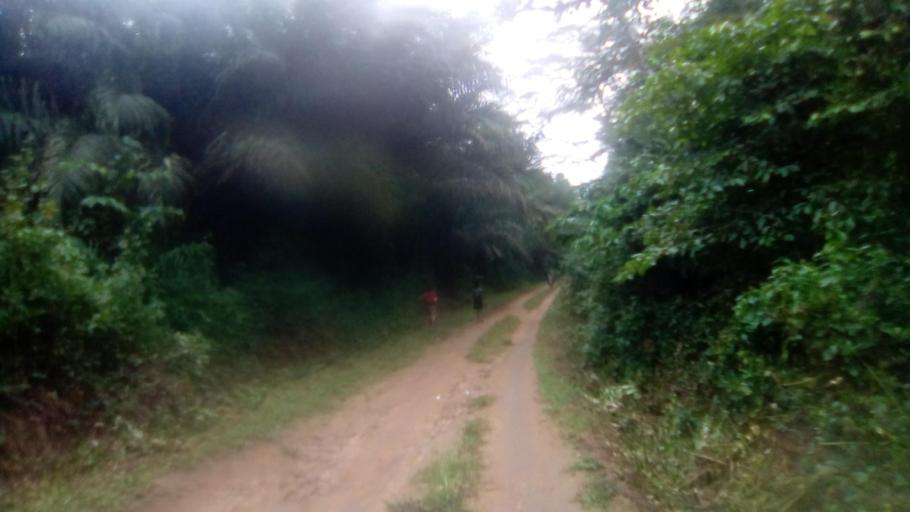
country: SL
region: Eastern Province
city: Kailahun
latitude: 8.2929
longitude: -10.6002
